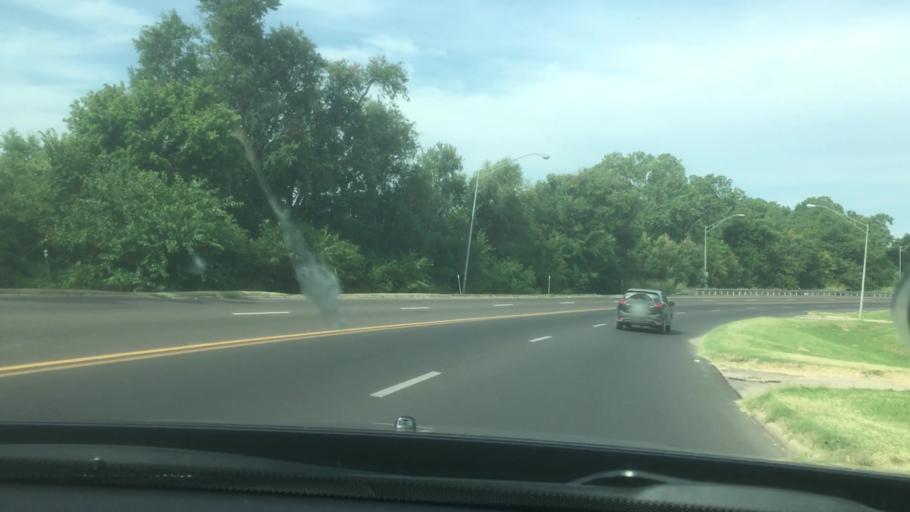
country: US
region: Oklahoma
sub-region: Garvin County
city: Pauls Valley
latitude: 34.7355
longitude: -97.2282
